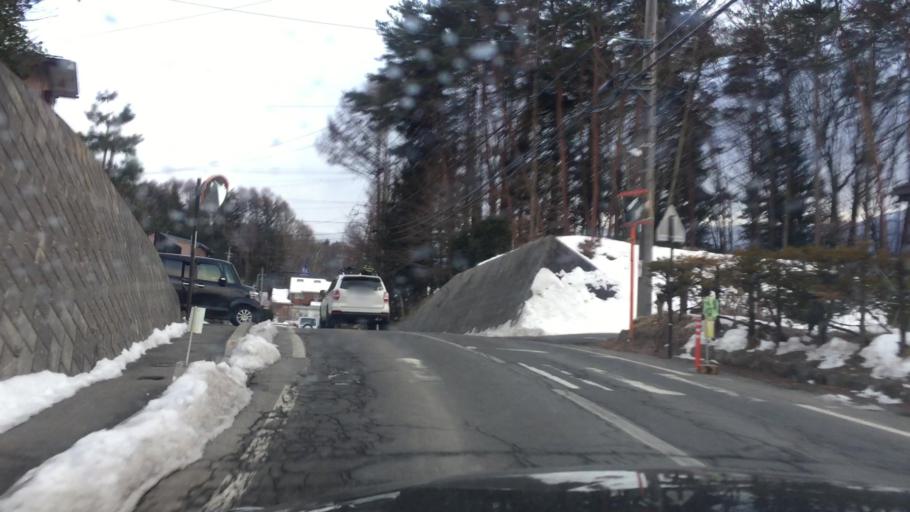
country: JP
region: Nagano
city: Chino
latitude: 35.9595
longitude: 138.2157
